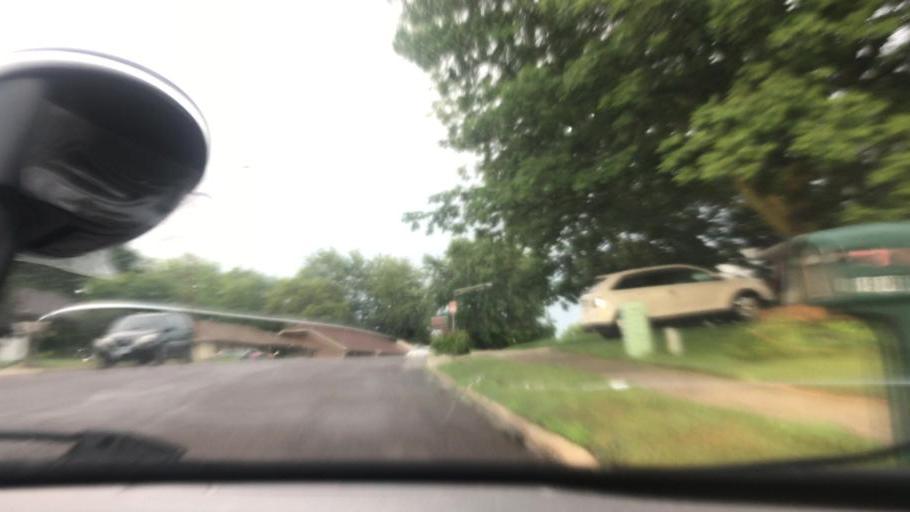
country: US
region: Illinois
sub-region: Tazewell County
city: Pekin
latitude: 40.5420
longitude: -89.6213
